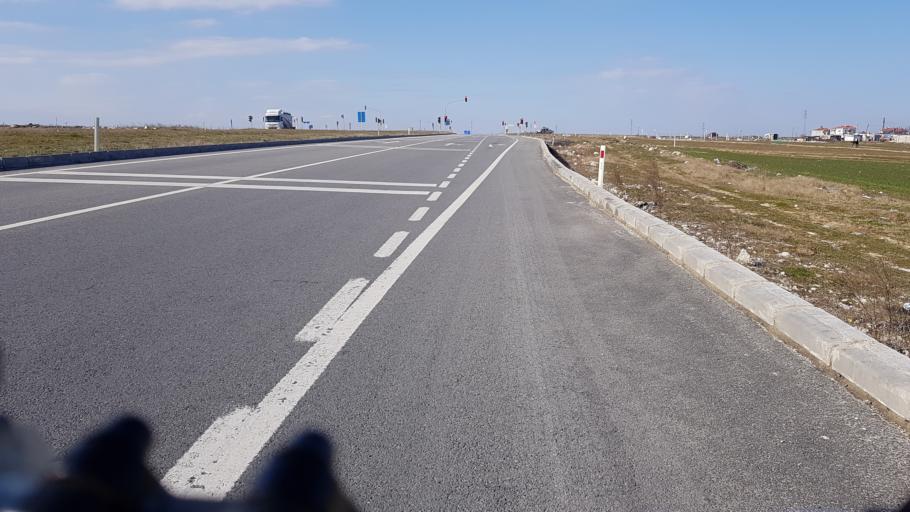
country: TR
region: Tekirdag
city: Saray
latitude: 41.4298
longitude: 27.9104
